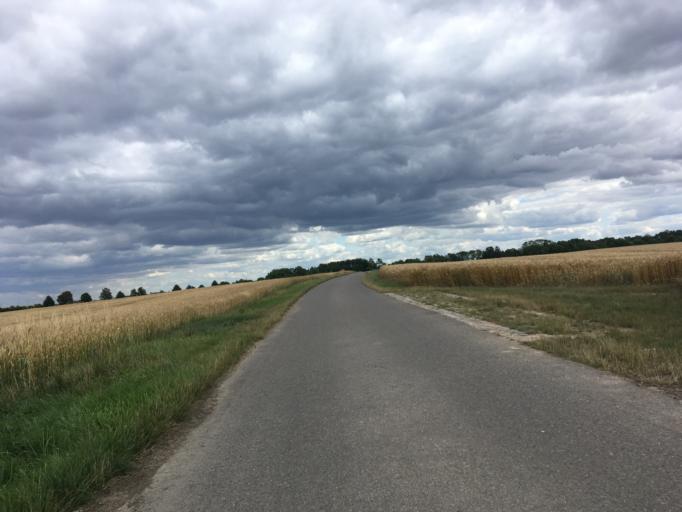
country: DE
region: Brandenburg
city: Gramzow
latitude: 53.2540
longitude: 13.9915
